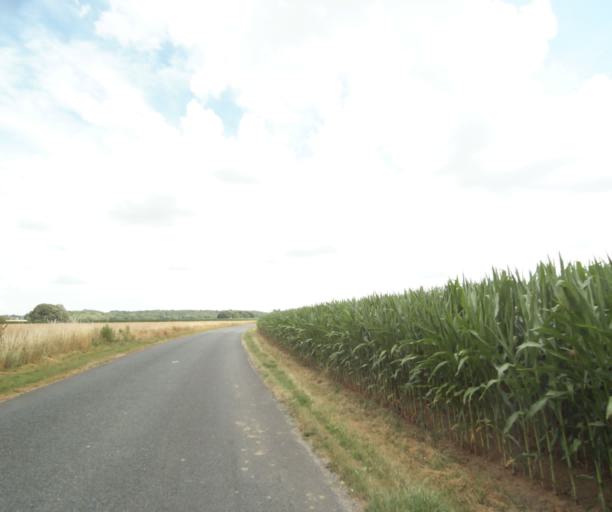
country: FR
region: Ile-de-France
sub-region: Departement de Seine-et-Marne
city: Hericy
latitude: 48.4449
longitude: 2.7797
